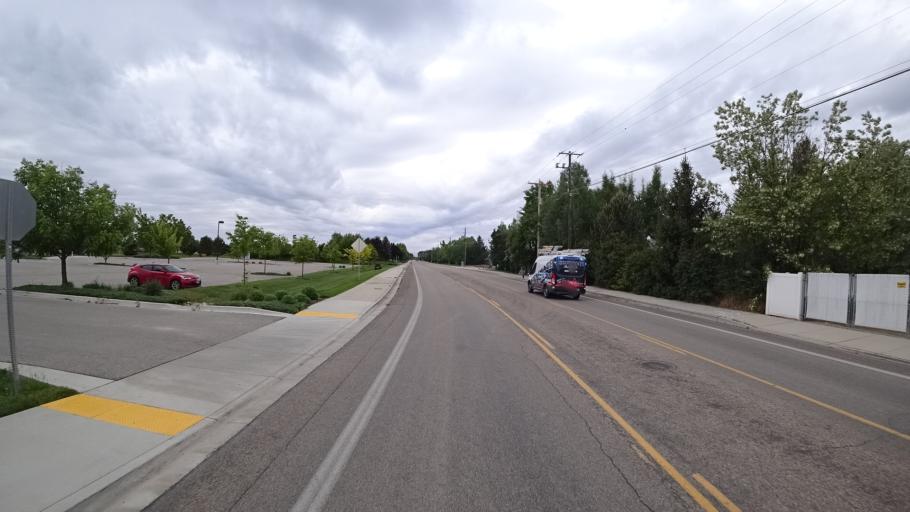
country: US
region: Idaho
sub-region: Ada County
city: Star
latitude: 43.7057
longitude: -116.4933
